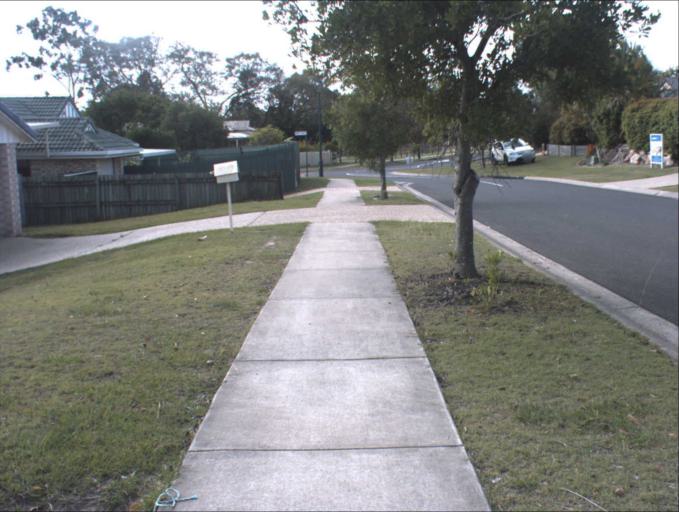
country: AU
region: Queensland
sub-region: Logan
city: Park Ridge South
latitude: -27.6887
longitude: 153.0514
